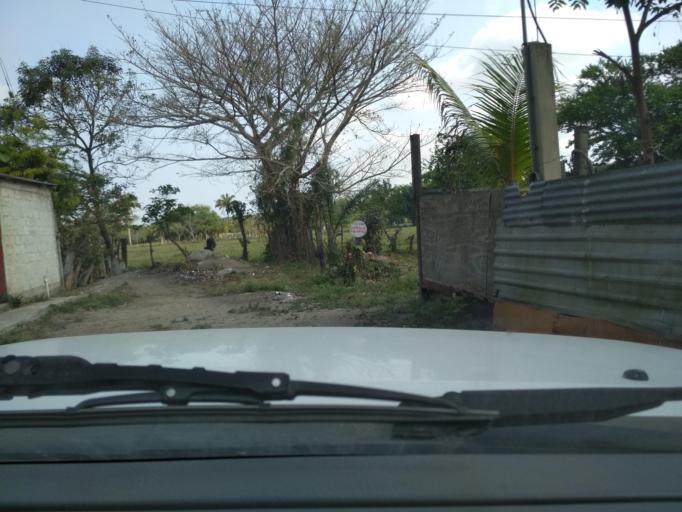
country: MX
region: Veracruz
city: El Tejar
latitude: 19.0819
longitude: -96.1642
